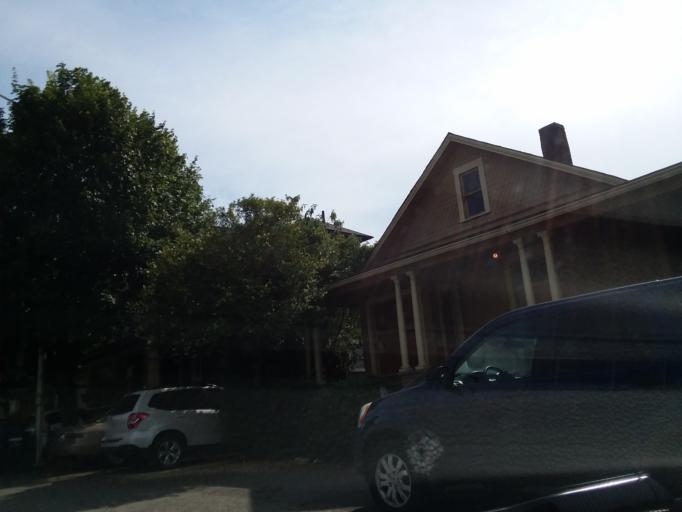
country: US
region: Washington
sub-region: King County
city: Seattle
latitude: 47.6395
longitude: -122.3236
